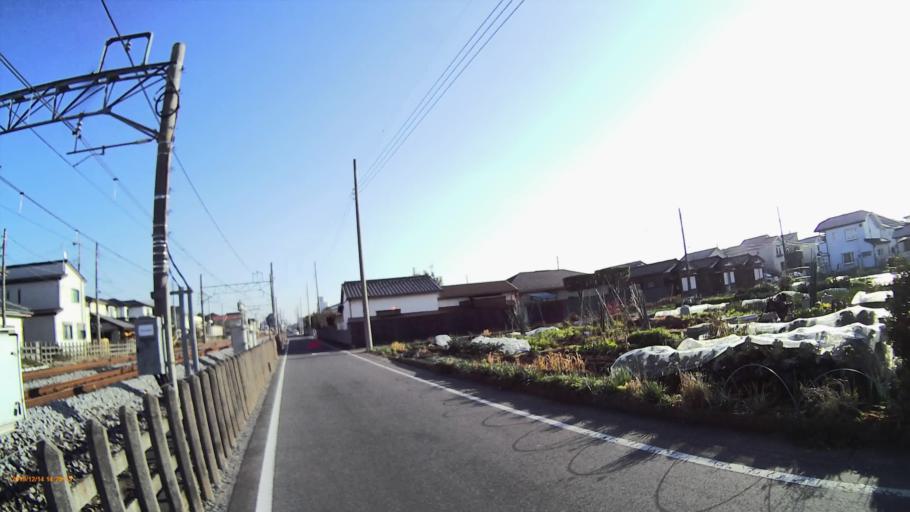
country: JP
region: Saitama
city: Konosu
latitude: 36.0382
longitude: 139.5291
